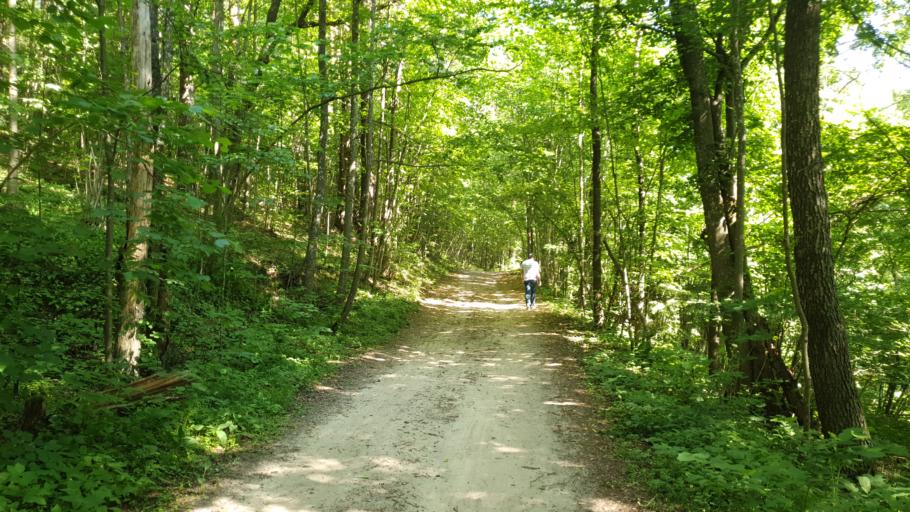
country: LT
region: Vilnius County
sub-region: Vilnius
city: Fabijoniskes
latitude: 54.7903
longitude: 25.3108
